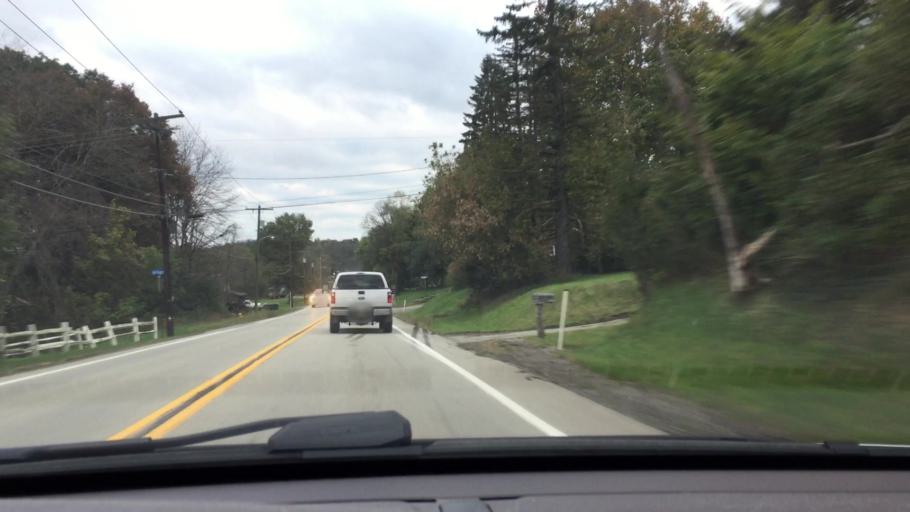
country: US
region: Pennsylvania
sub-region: Washington County
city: Canonsburg
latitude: 40.2102
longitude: -80.1305
